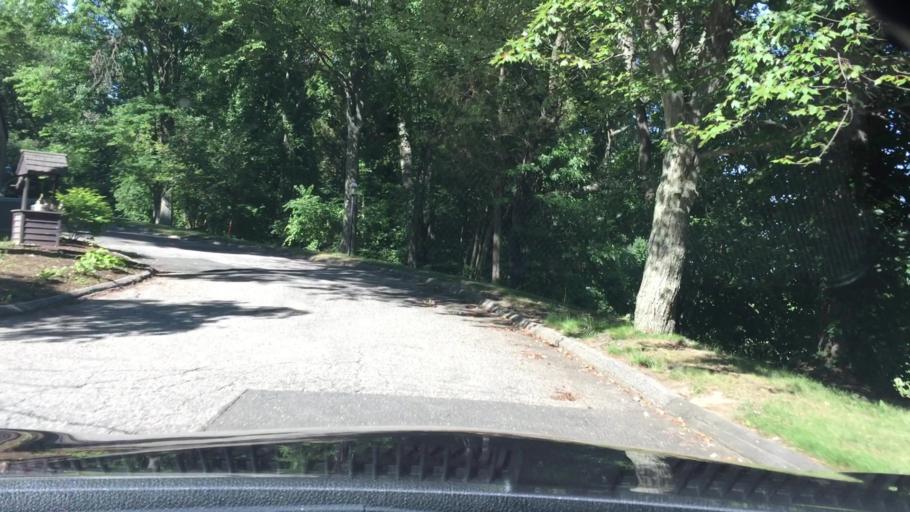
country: US
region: Connecticut
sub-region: New Haven County
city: City of Milford (balance)
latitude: 41.2451
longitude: -73.1070
